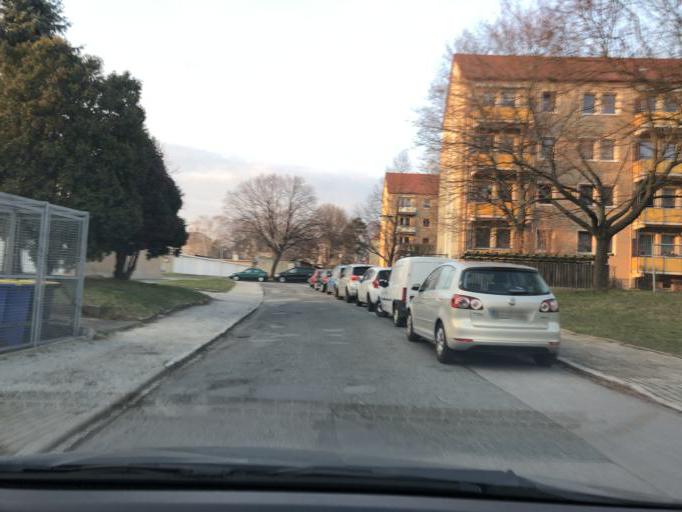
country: DE
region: Saxony
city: Bautzen
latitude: 51.1787
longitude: 14.4418
